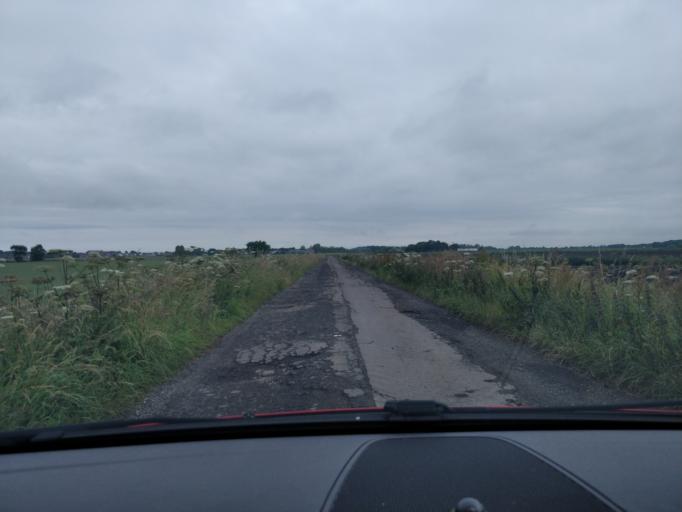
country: GB
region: England
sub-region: Lancashire
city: Banks
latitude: 53.6619
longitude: -2.9332
